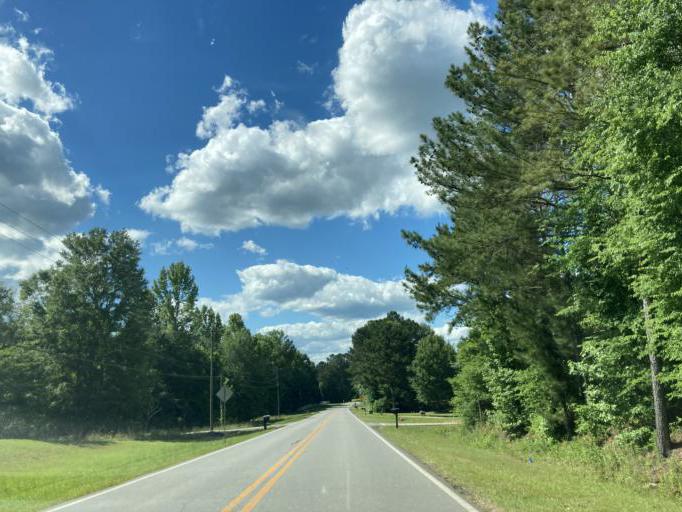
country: US
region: Georgia
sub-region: Jones County
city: Gray
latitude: 32.9822
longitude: -83.5494
